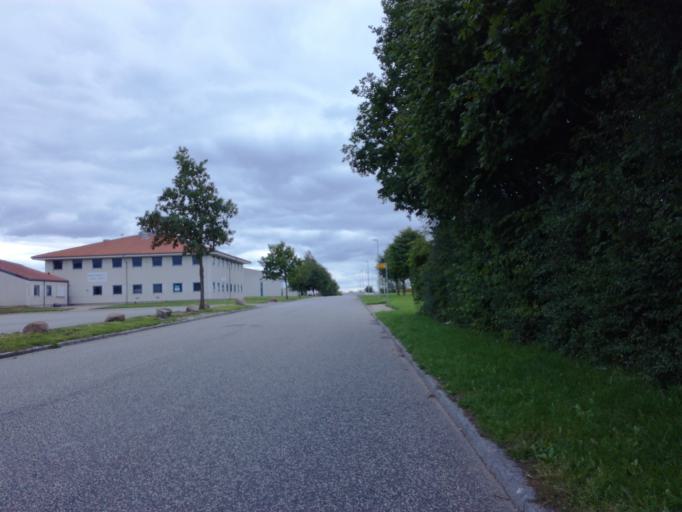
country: DK
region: South Denmark
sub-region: Vejle Kommune
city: Vejle
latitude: 55.6784
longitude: 9.5869
